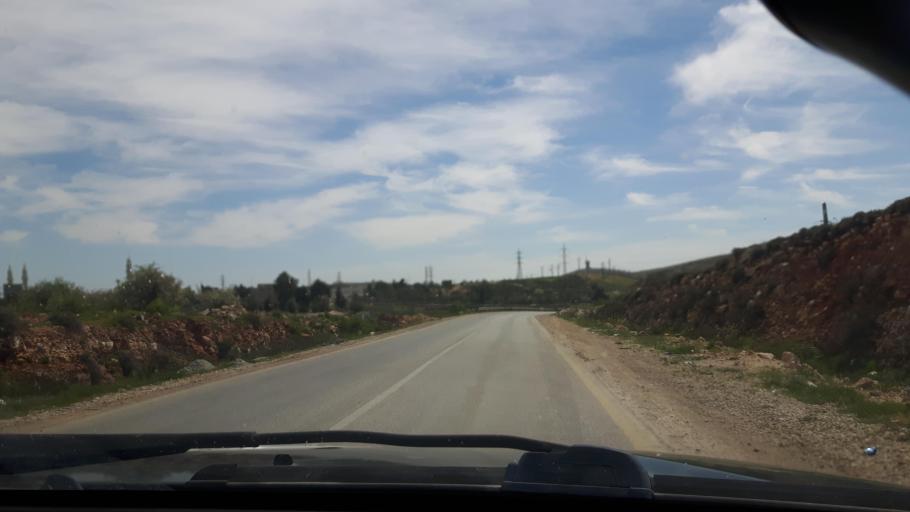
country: PS
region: West Bank
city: Qalandiya
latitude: 31.8643
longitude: 35.2021
